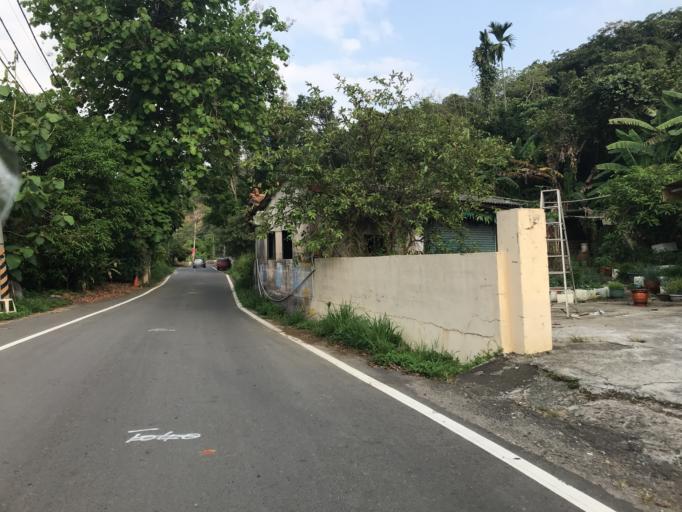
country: TW
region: Taiwan
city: Zhongxing New Village
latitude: 24.0381
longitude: 120.7100
